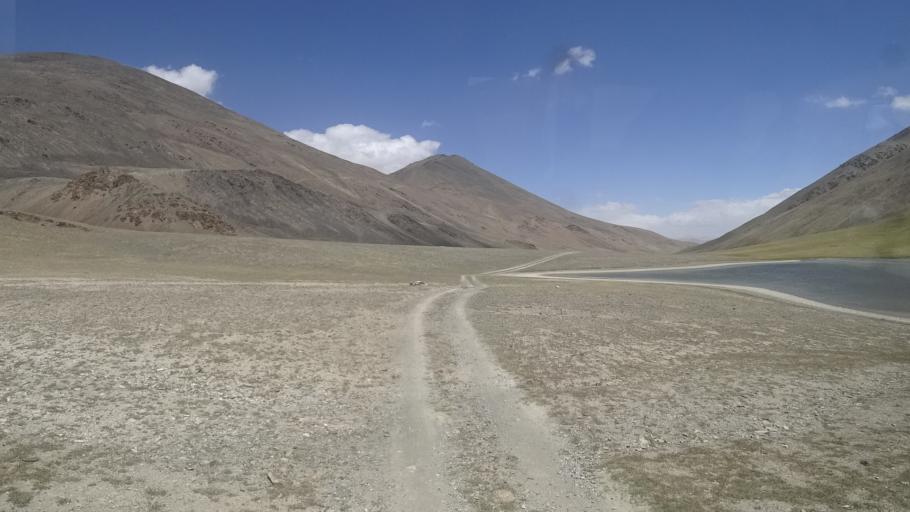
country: TJ
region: Gorno-Badakhshan
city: Murghob
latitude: 37.5212
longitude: 74.0613
